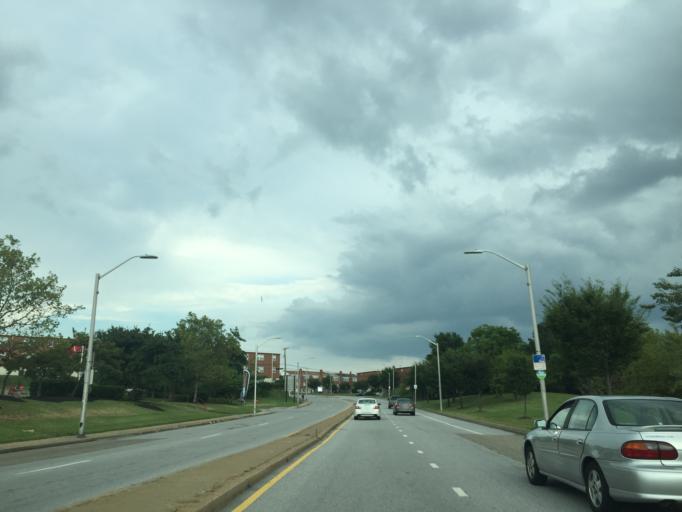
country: US
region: Maryland
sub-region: Baltimore County
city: Dundalk
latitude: 39.2787
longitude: -76.5475
